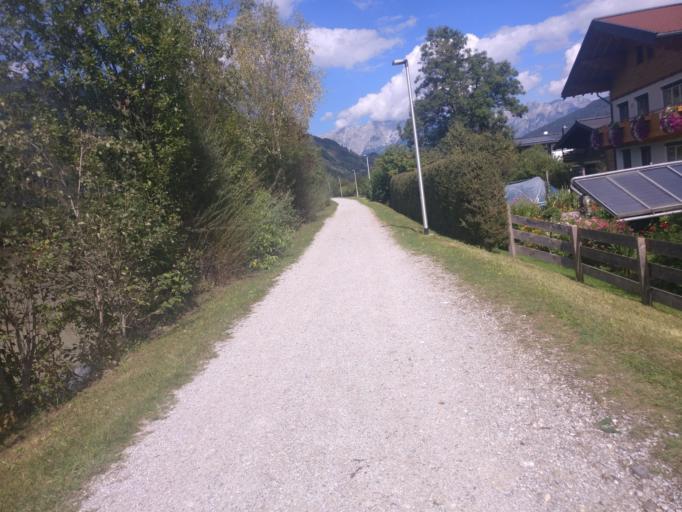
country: AT
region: Salzburg
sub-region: Politischer Bezirk Sankt Johann im Pongau
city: Sankt Johann im Pongau
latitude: 47.3625
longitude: 13.2083
